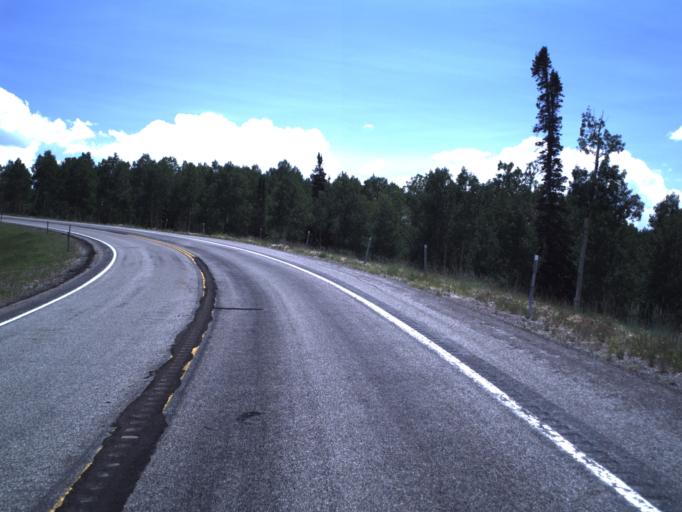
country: US
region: Utah
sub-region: Sanpete County
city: Fairview
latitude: 39.6255
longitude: -111.3213
